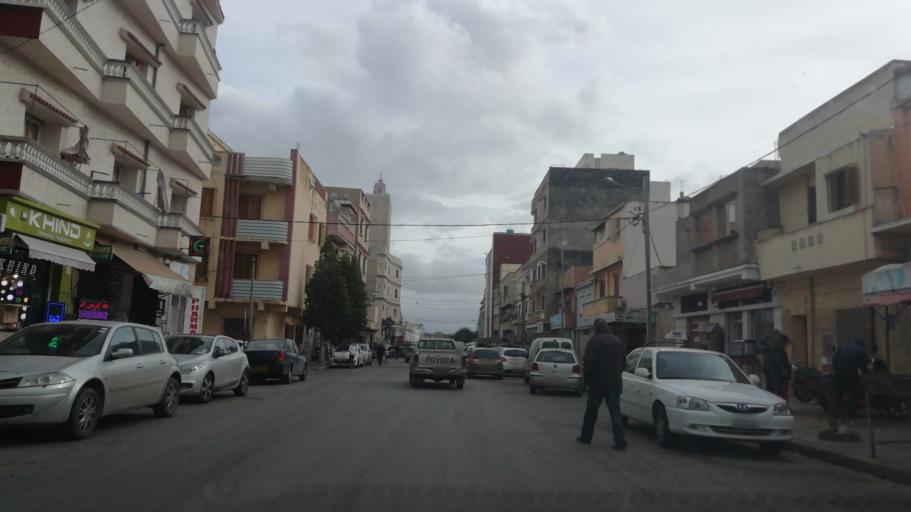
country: DZ
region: Oran
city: Oran
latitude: 35.6849
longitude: -0.6428
